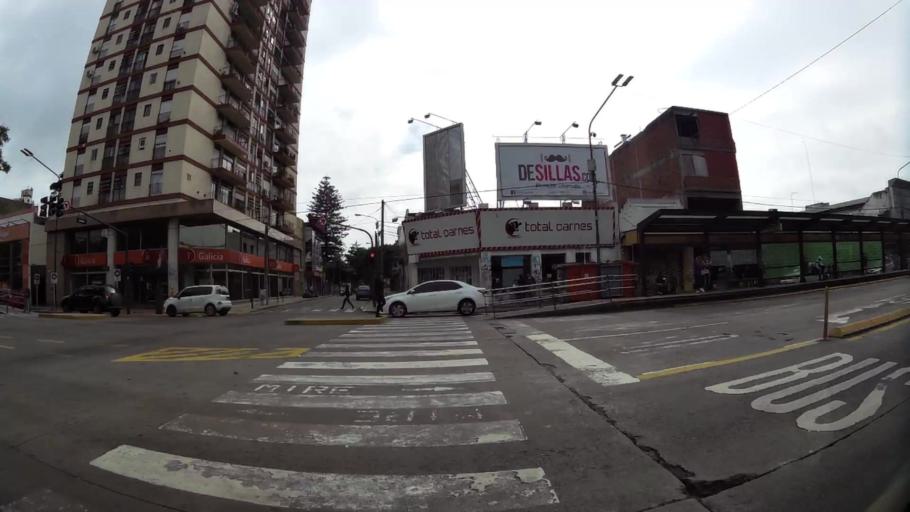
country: AR
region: Buenos Aires
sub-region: Partido de Vicente Lopez
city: Olivos
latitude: -34.5355
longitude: -58.4777
